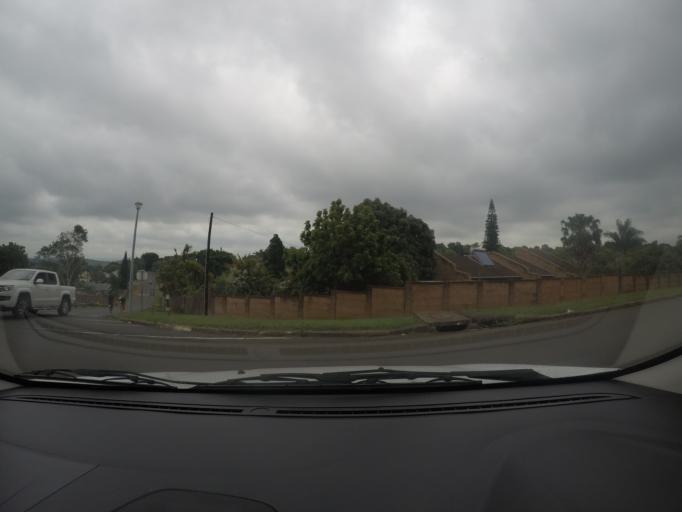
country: ZA
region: KwaZulu-Natal
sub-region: uThungulu District Municipality
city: Empangeni
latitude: -28.7684
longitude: 31.8950
